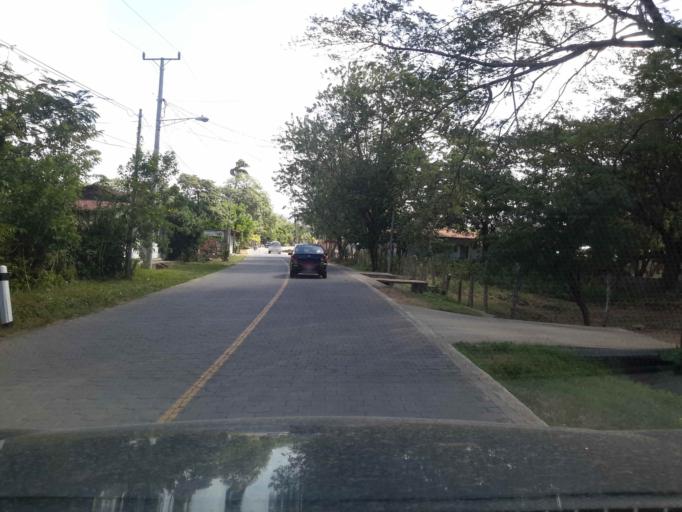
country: NI
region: Rivas
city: San Juan del Sur
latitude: 11.2543
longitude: -85.8582
